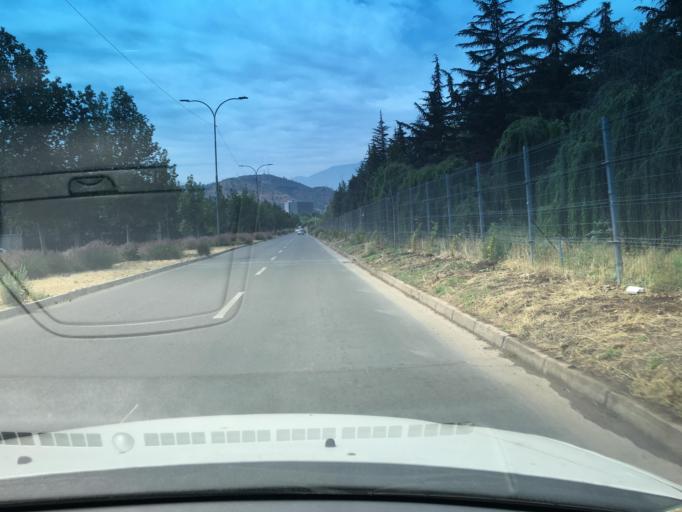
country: CL
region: Santiago Metropolitan
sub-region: Provincia de Santiago
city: Santiago
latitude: -33.3814
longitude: -70.6349
